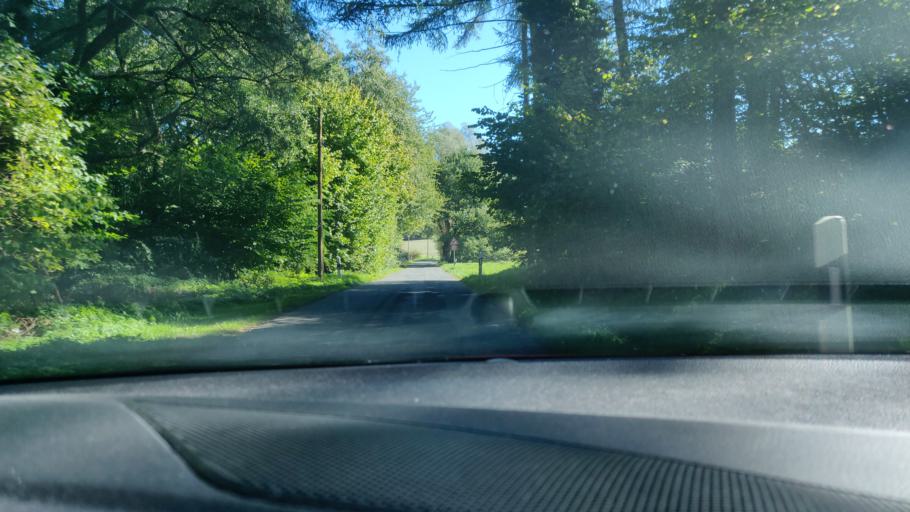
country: DE
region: North Rhine-Westphalia
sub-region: Regierungsbezirk Dusseldorf
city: Velbert
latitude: 51.3566
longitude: 7.0698
